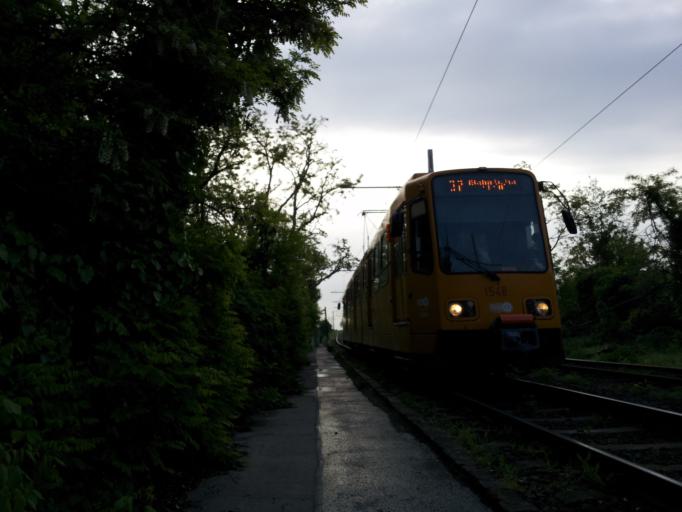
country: HU
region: Budapest
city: Budapest XIV. keruelet
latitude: 47.4908
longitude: 19.0997
